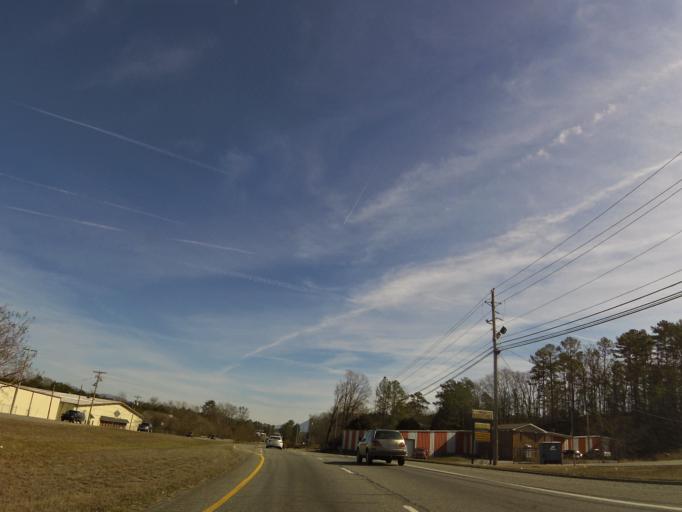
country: US
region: Georgia
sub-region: Murray County
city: Chatsworth
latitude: 34.7809
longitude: -84.8619
